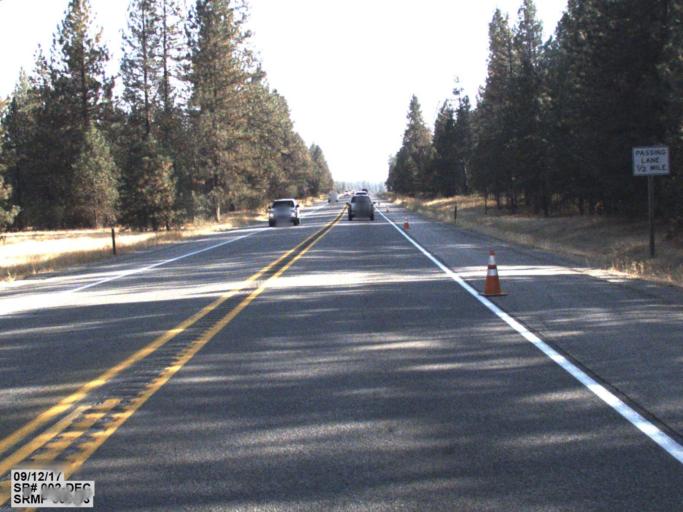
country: US
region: Washington
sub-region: Spokane County
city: Deer Park
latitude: 47.9203
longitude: -117.3501
